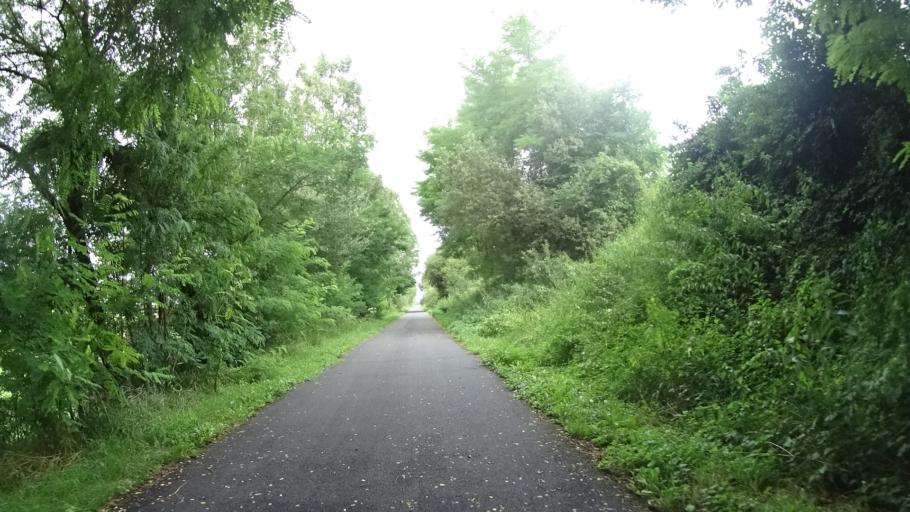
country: FR
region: Lorraine
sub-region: Departement de la Moselle
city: Lorquin
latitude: 48.6953
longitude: 7.0291
